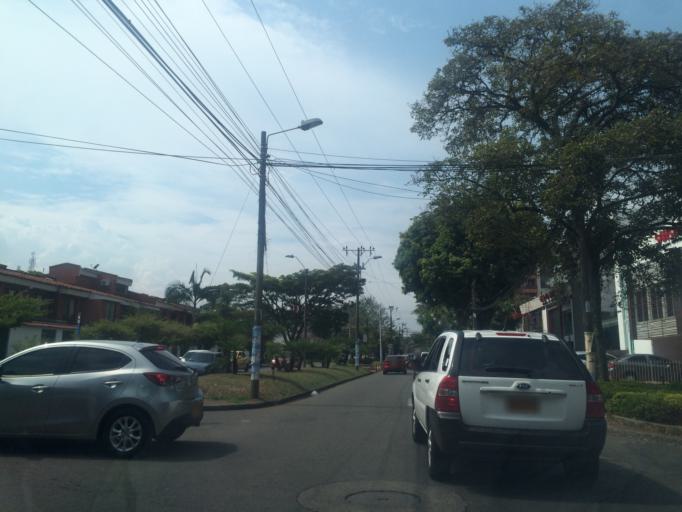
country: CO
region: Valle del Cauca
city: Cali
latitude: 3.3683
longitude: -76.5371
